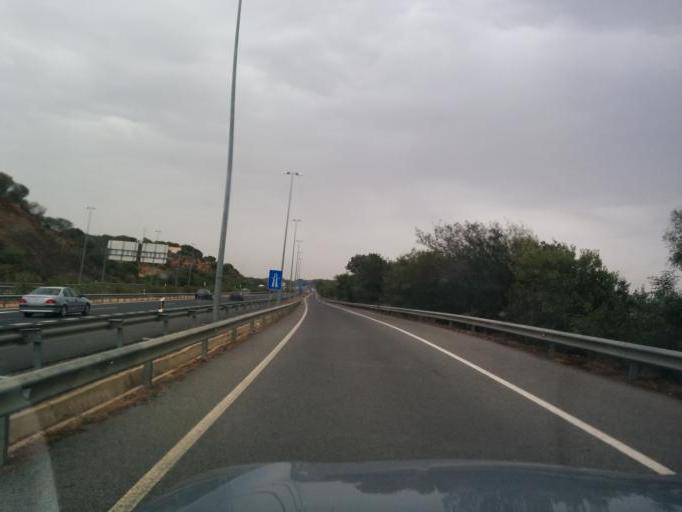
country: ES
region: Andalusia
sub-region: Provincia de Huelva
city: Ayamonte
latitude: 37.2383
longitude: -7.3992
